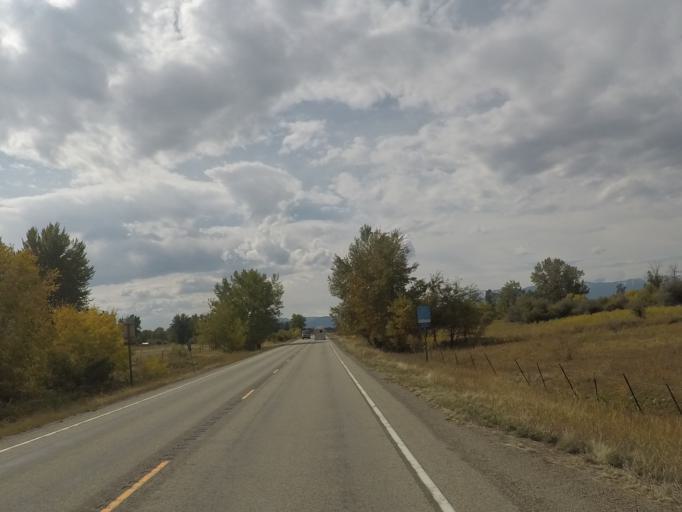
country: US
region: Montana
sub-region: Carbon County
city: Red Lodge
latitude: 45.3428
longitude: -109.1783
